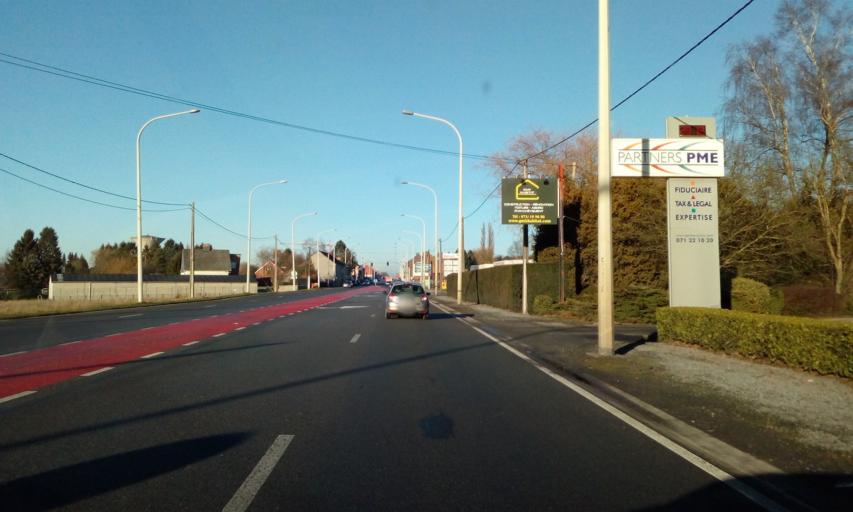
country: BE
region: Wallonia
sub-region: Province du Hainaut
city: Gerpinnes
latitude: 50.3353
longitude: 4.4750
